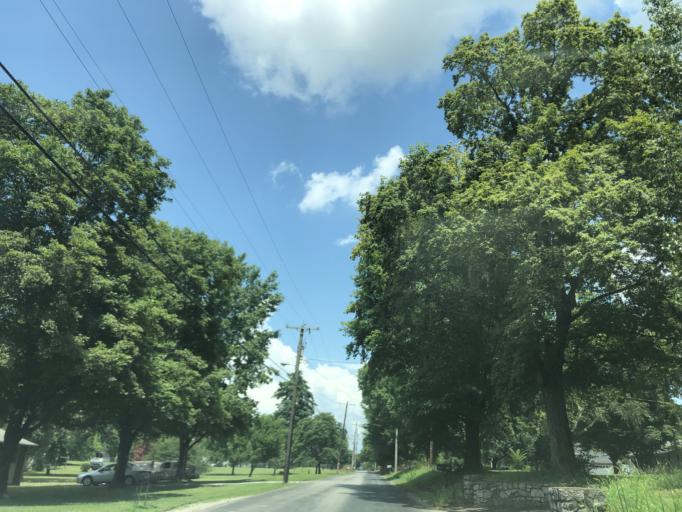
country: US
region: Tennessee
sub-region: Davidson County
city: Lakewood
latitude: 36.2028
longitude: -86.6195
